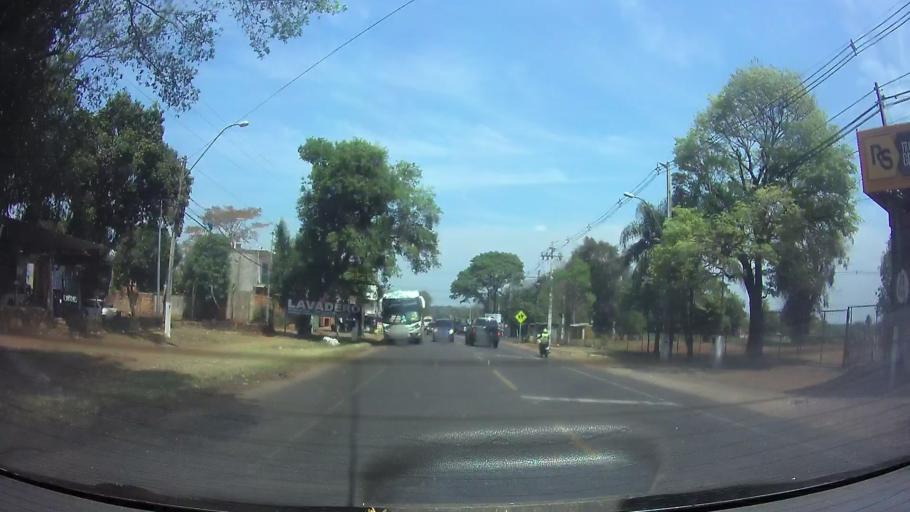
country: PY
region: Central
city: Capiata
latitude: -25.3835
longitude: -57.4730
